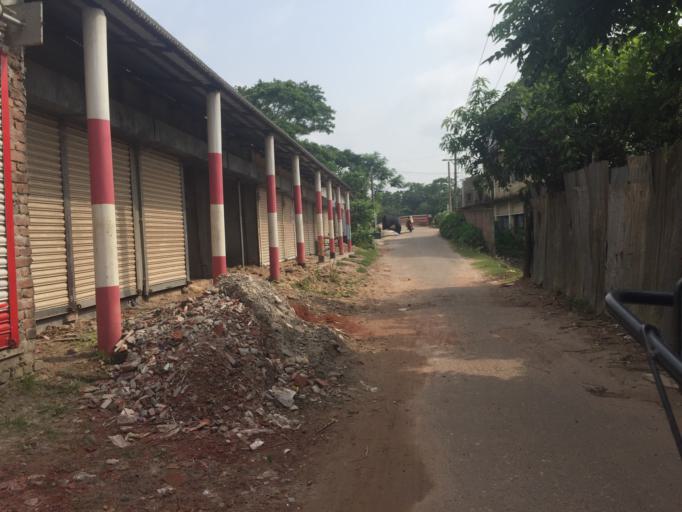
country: BD
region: Barisal
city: Mathba
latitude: 22.2158
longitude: 89.9133
